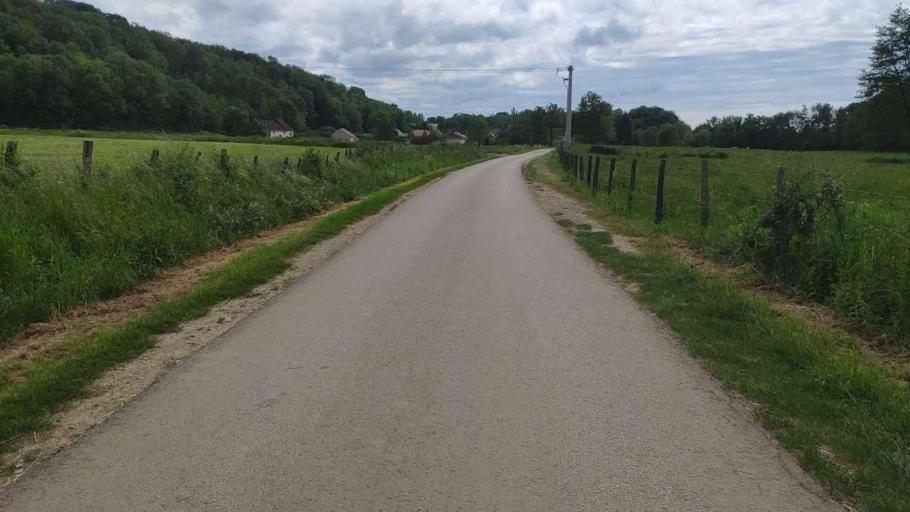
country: FR
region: Franche-Comte
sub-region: Departement du Jura
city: Montmorot
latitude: 46.7379
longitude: 5.5301
